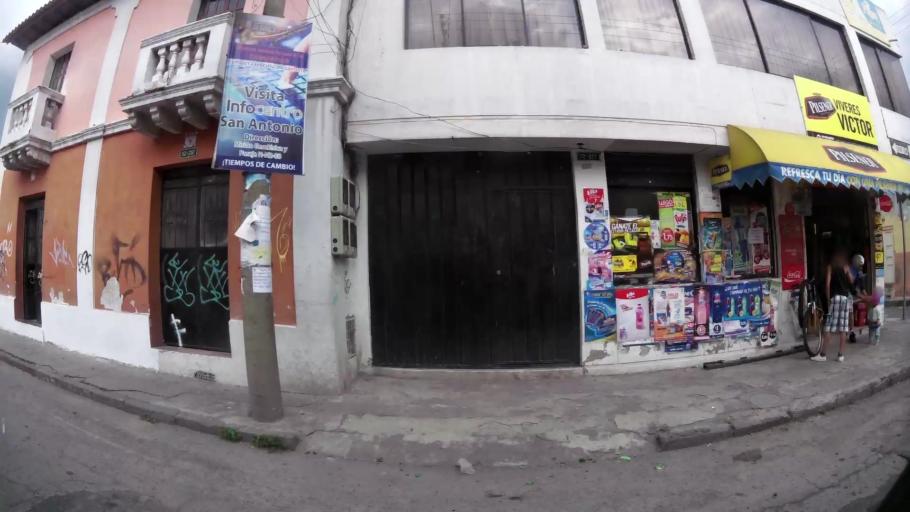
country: EC
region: Pichincha
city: Quito
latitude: -0.0128
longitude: -78.4485
